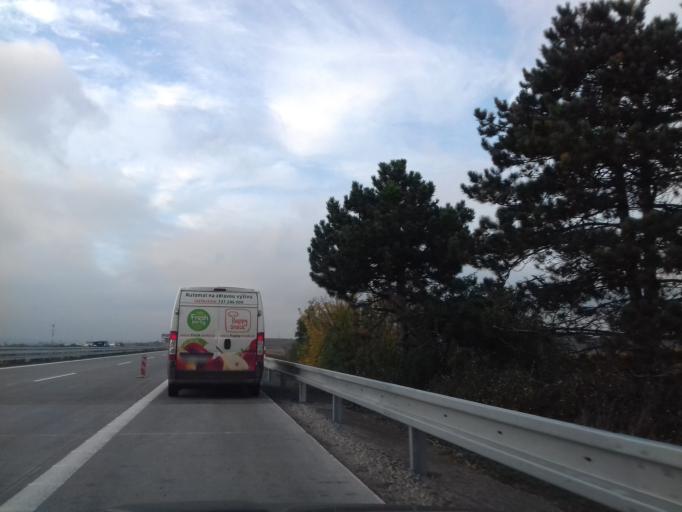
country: CZ
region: South Moravian
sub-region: Okres Brno-Venkov
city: Blucina
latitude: 49.0476
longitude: 16.6760
